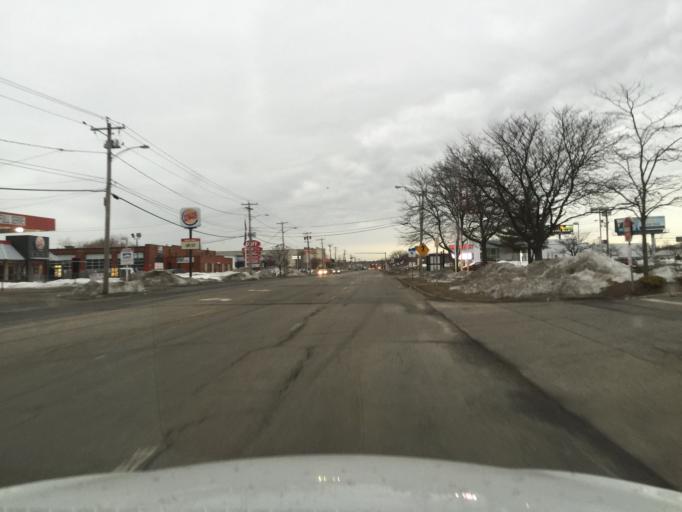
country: US
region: Massachusetts
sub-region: Middlesex County
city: Somerville
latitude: 42.4017
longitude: -71.0977
